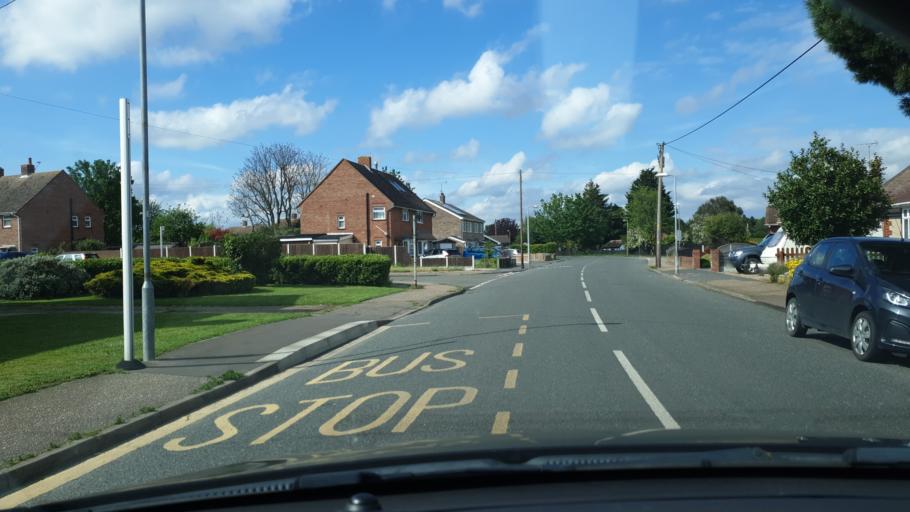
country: GB
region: England
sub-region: Essex
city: Brightlingsea
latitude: 51.8155
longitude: 1.0330
